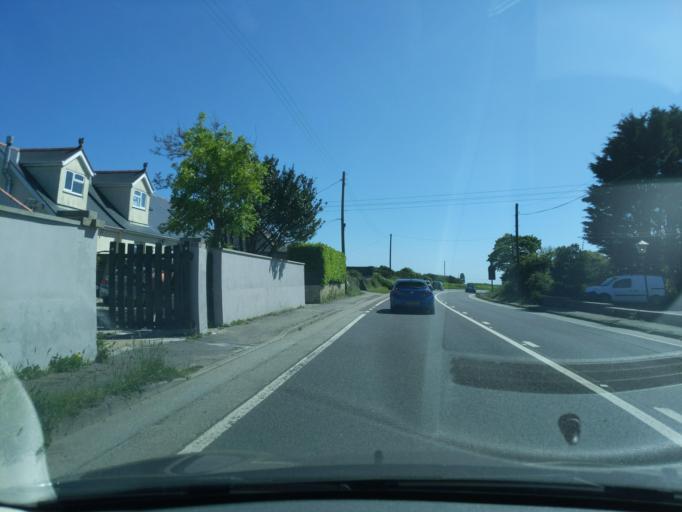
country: GB
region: England
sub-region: Cornwall
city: Wendron
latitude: 50.1590
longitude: -5.1861
